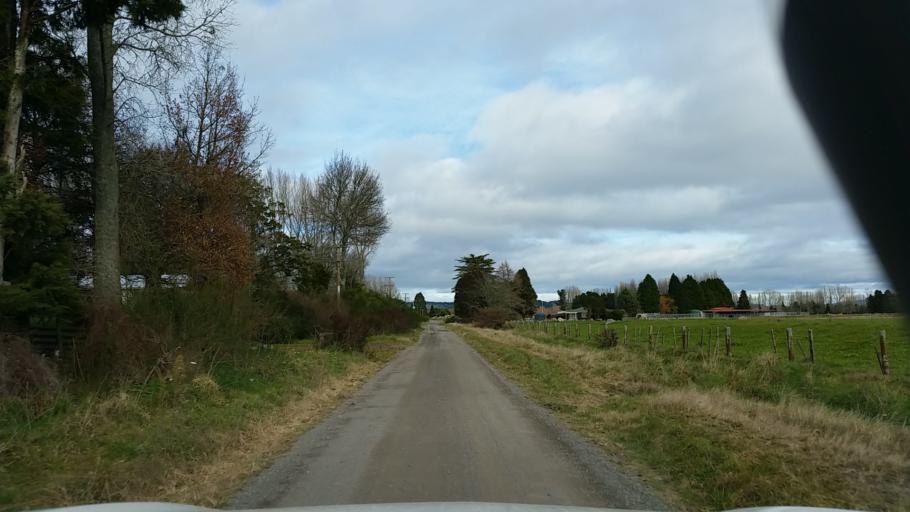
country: NZ
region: Bay of Plenty
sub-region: Kawerau District
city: Kawerau
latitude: -38.2822
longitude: 176.5521
